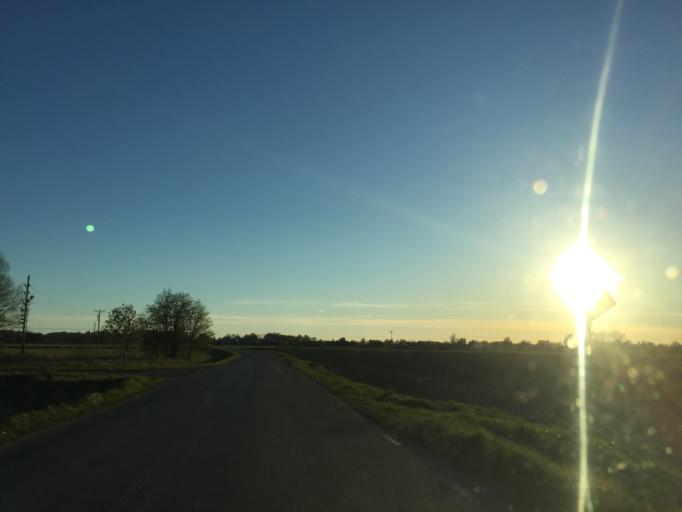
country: SE
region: OErebro
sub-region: Orebro Kommun
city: Odensbacken
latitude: 59.2051
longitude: 15.5183
